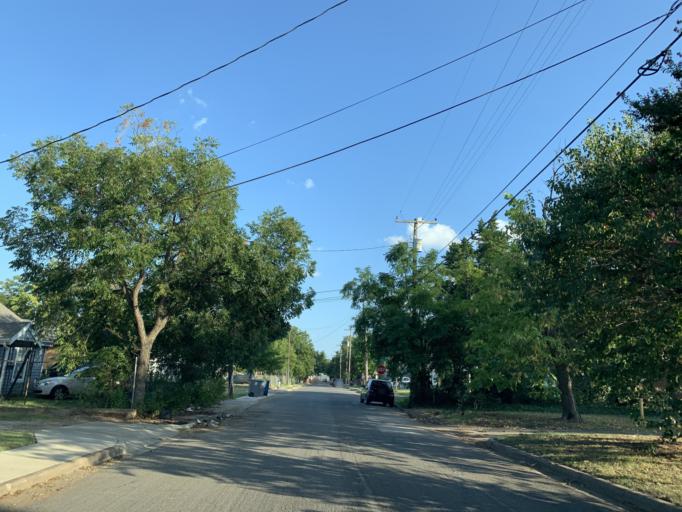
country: US
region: Texas
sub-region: Dallas County
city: Dallas
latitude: 32.7024
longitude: -96.7814
